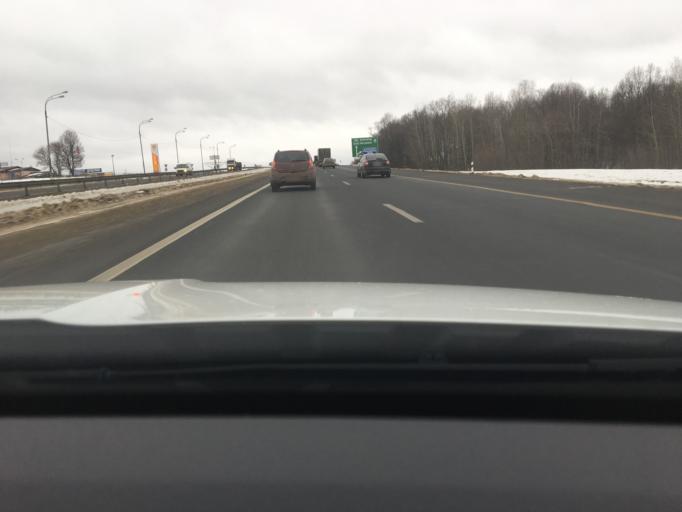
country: RU
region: Moskovskaya
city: Serpukhov
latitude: 54.8477
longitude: 37.4668
